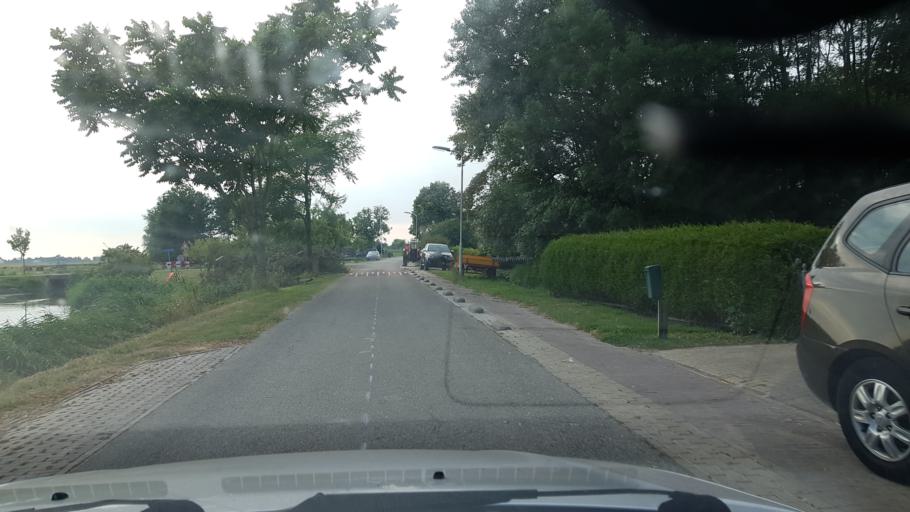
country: NL
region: Friesland
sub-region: Gemeente Dongeradeel
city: Holwerd
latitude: 53.3464
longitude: 5.8755
